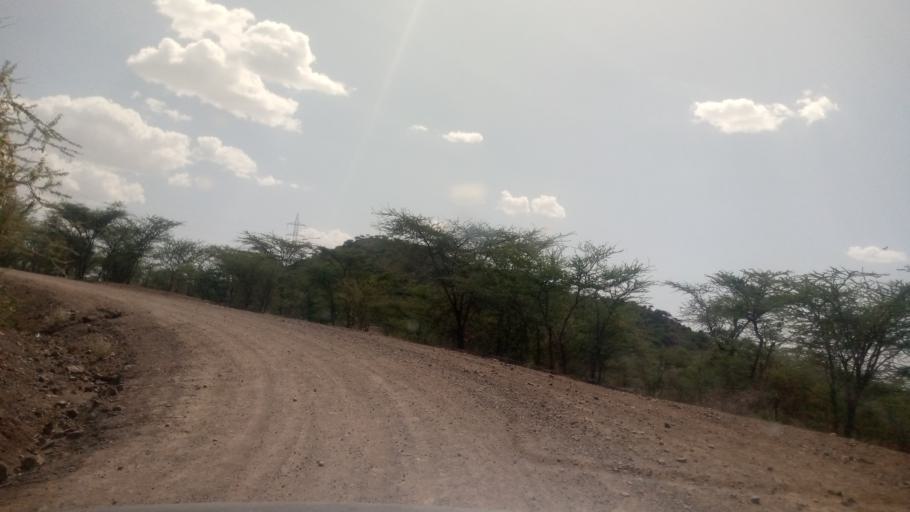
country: ET
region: Oromiya
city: Deder
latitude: 9.5254
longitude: 41.2271
